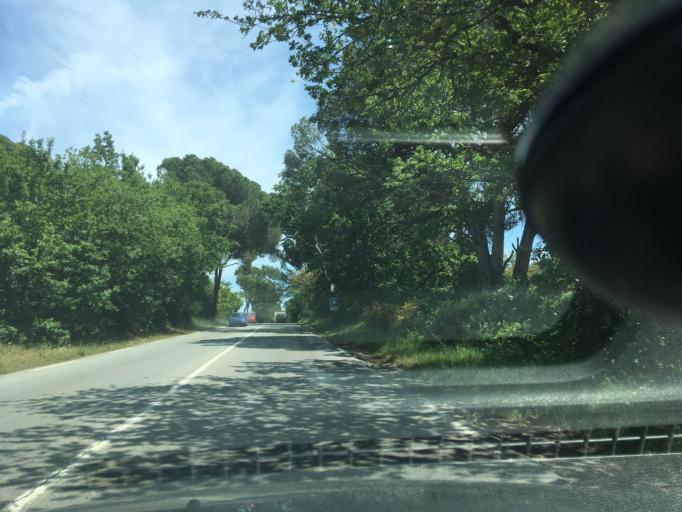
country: FR
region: Provence-Alpes-Cote d'Azur
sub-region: Departement du Var
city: Puget-sur-Argens
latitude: 43.4610
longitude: 6.6603
